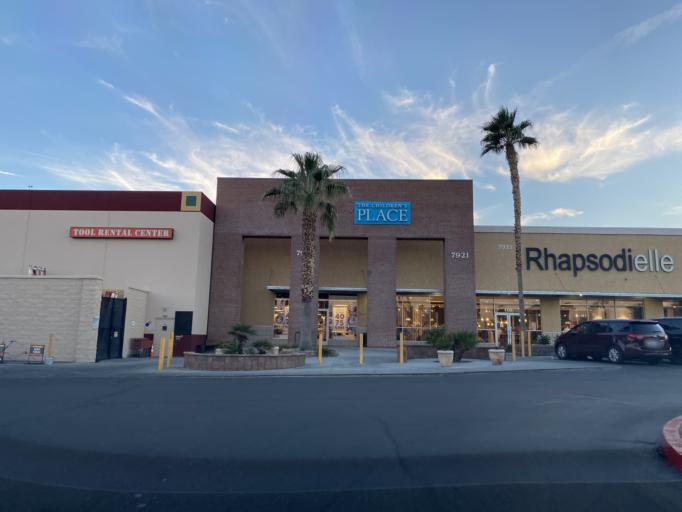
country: US
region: Nevada
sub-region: Clark County
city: Las Vegas
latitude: 36.2699
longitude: -115.2670
